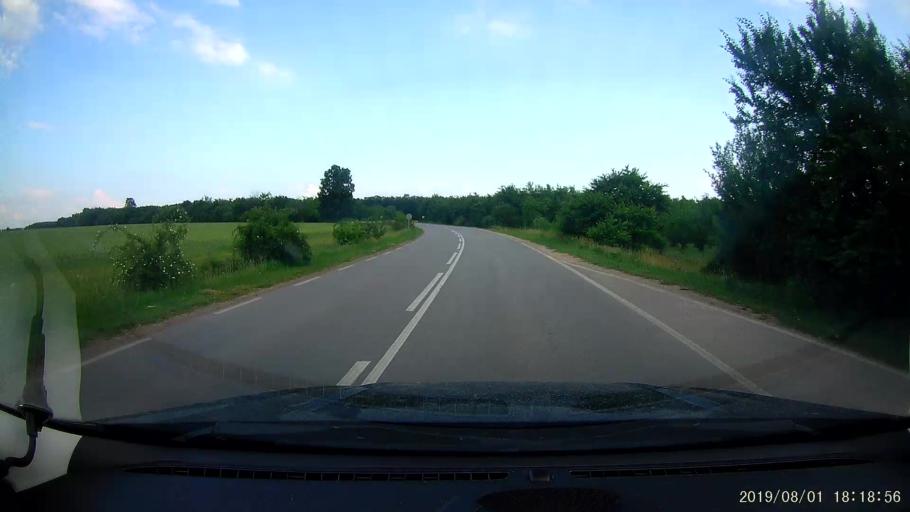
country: BG
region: Shumen
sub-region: Obshtina Kaolinovo
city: Kaolinovo
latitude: 43.6906
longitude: 27.0862
